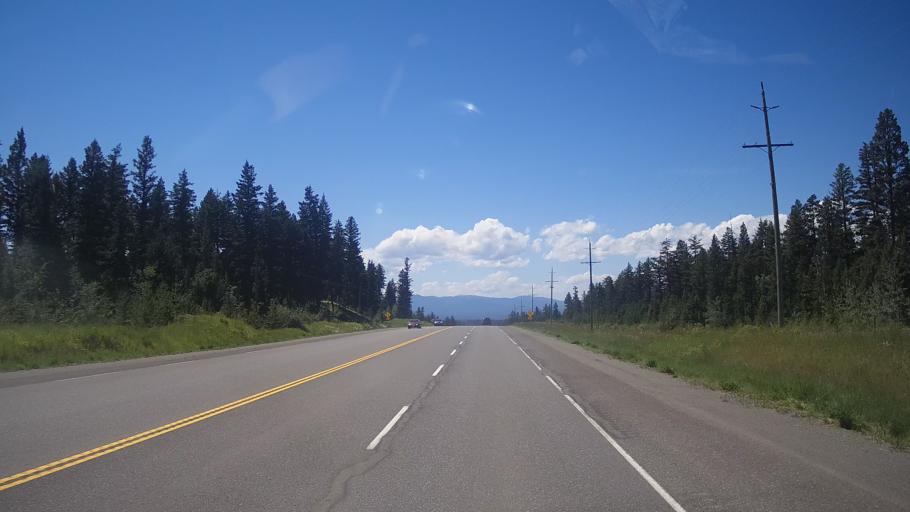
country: CA
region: British Columbia
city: Cache Creek
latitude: 51.2709
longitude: -121.4476
